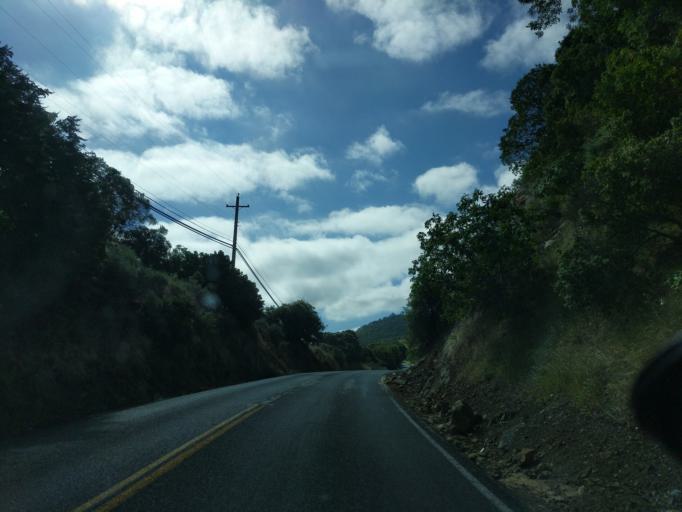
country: US
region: California
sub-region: Contra Costa County
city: Clayton
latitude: 37.9195
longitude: -121.8973
